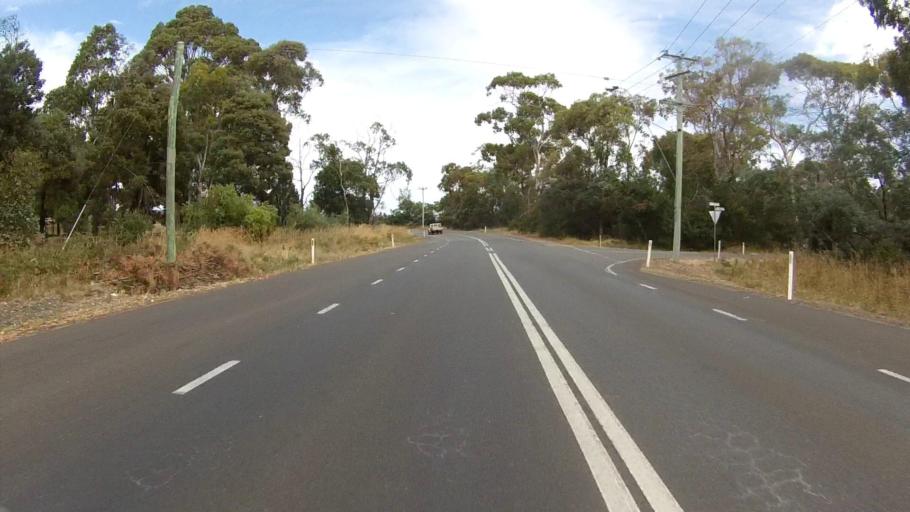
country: AU
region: Tasmania
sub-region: Clarence
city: Sandford
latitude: -42.9292
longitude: 147.4915
